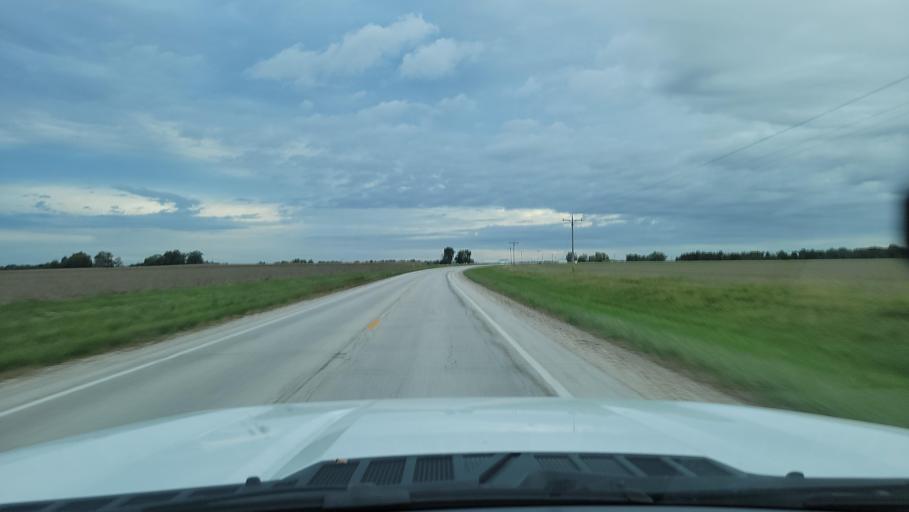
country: US
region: Illinois
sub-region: Schuyler County
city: Rushville
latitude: 40.0742
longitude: -90.6151
